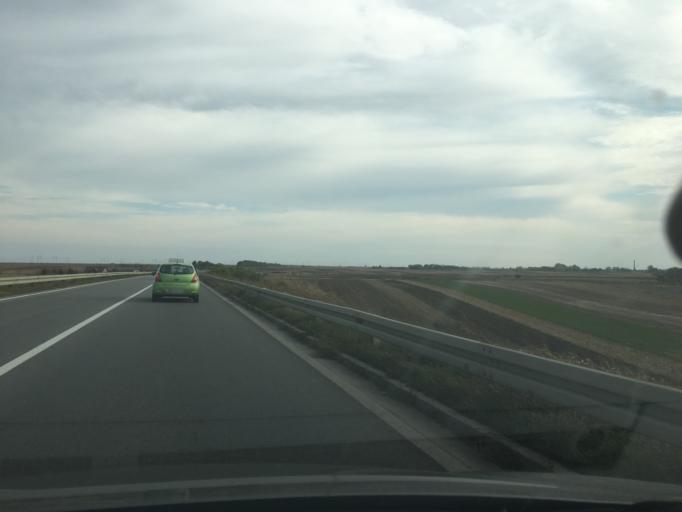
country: RS
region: Autonomna Pokrajina Vojvodina
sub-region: Juznobacki Okrug
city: Petrovaradin
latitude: 45.3148
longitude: 19.9189
